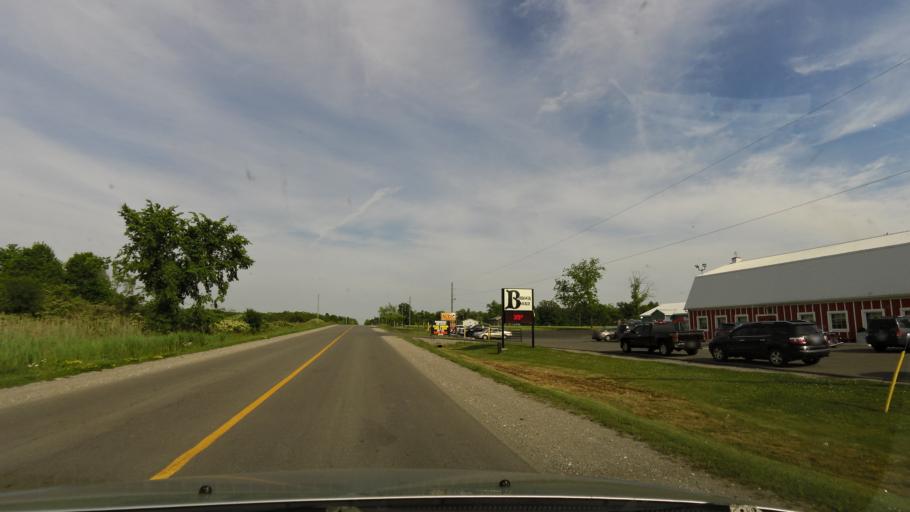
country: CA
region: Ontario
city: Ancaster
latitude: 43.0449
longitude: -80.0537
